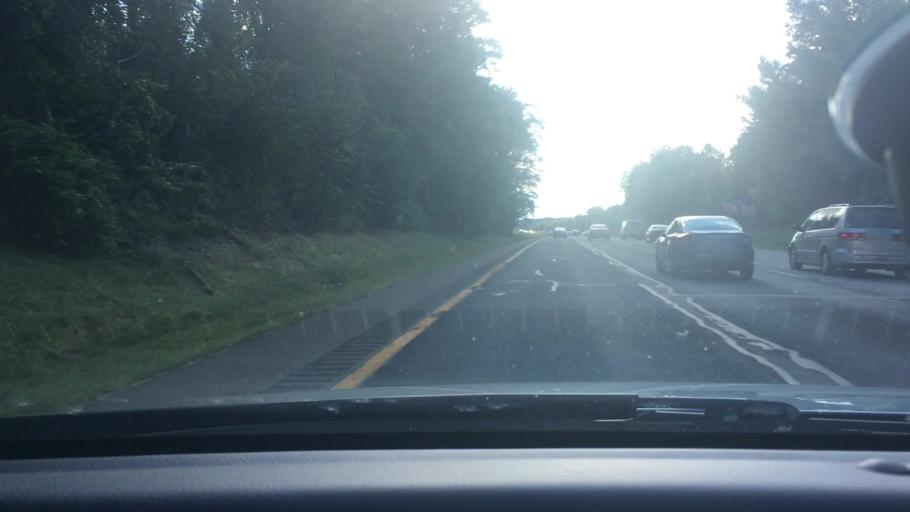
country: US
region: New Jersey
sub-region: Morris County
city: Boonton
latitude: 40.9105
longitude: -74.3863
